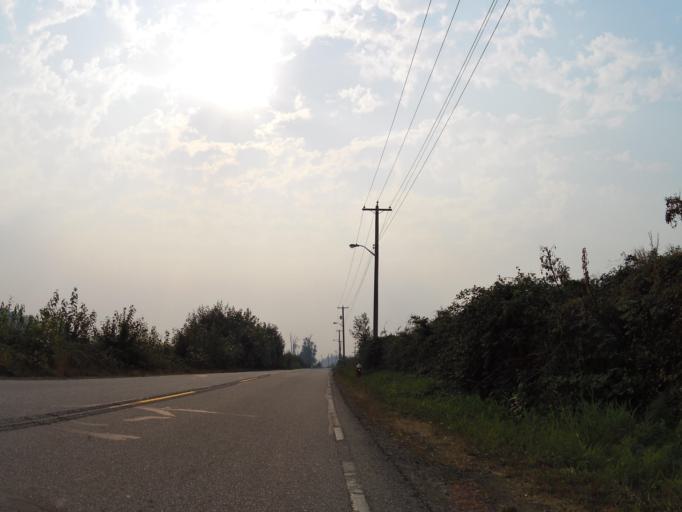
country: CA
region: British Columbia
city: Burnaby
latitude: 49.1901
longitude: -123.0028
